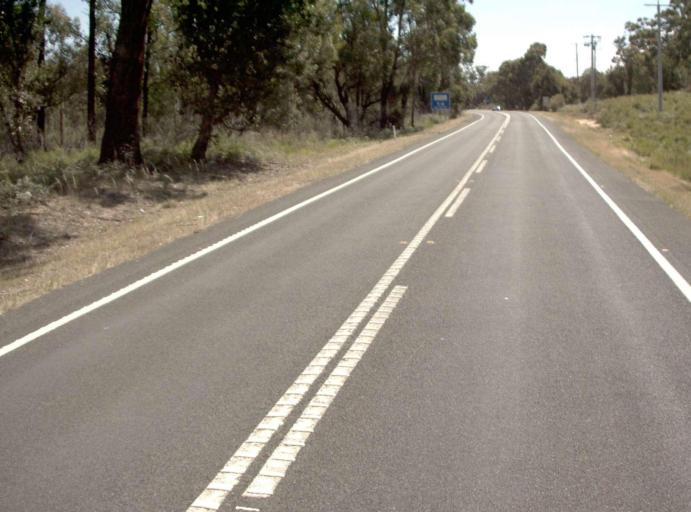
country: AU
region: Victoria
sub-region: Wellington
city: Sale
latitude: -37.9163
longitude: 147.2934
